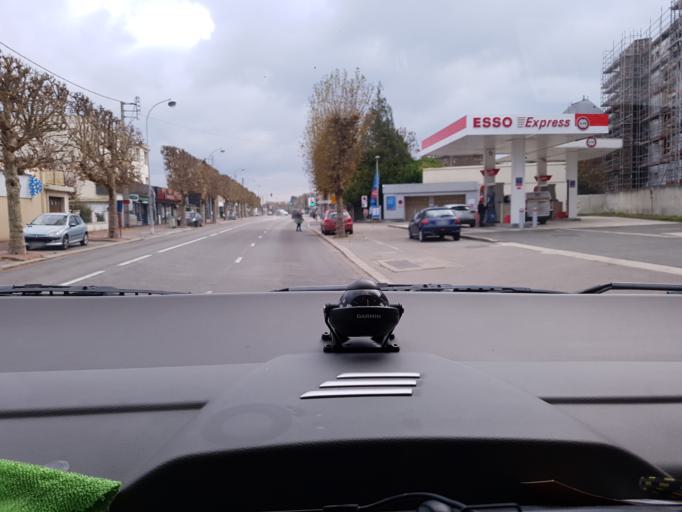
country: FR
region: Haute-Normandie
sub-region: Departement de la Seine-Maritime
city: Rouxmesnil-Bouteilles
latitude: 49.9164
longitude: 1.0744
